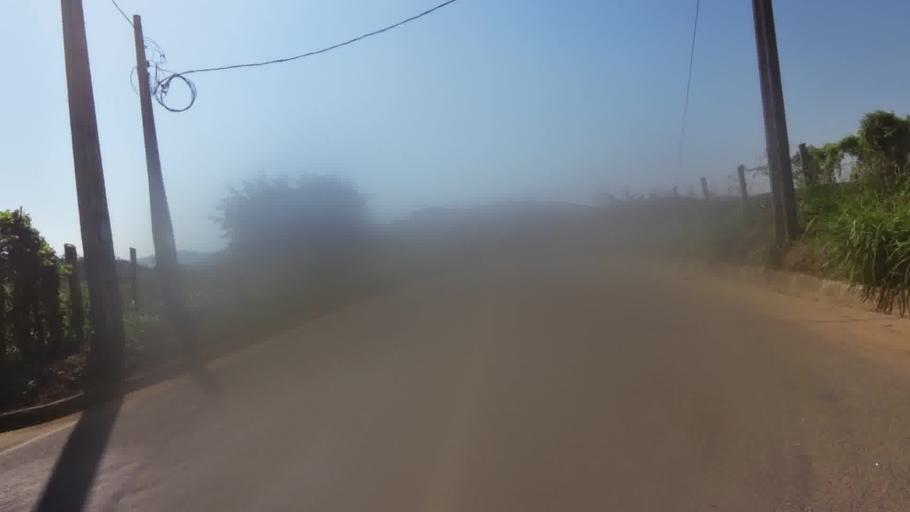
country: BR
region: Espirito Santo
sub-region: Alfredo Chaves
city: Alfredo Chaves
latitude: -20.6546
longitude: -40.7572
